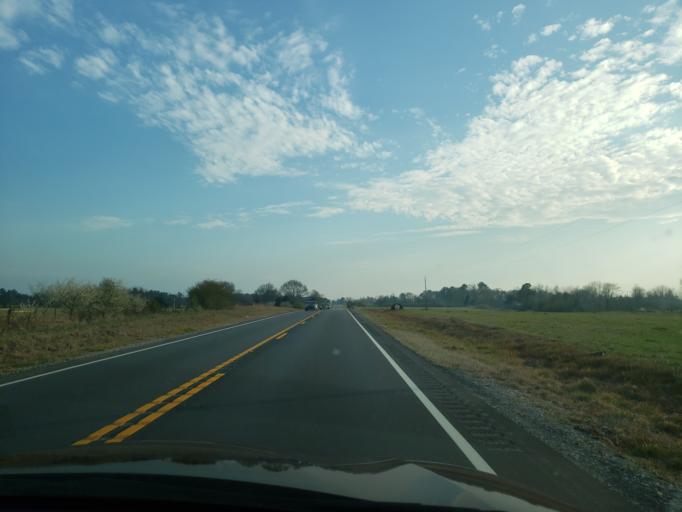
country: US
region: Alabama
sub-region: Hale County
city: Moundville
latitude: 32.8767
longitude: -87.6100
